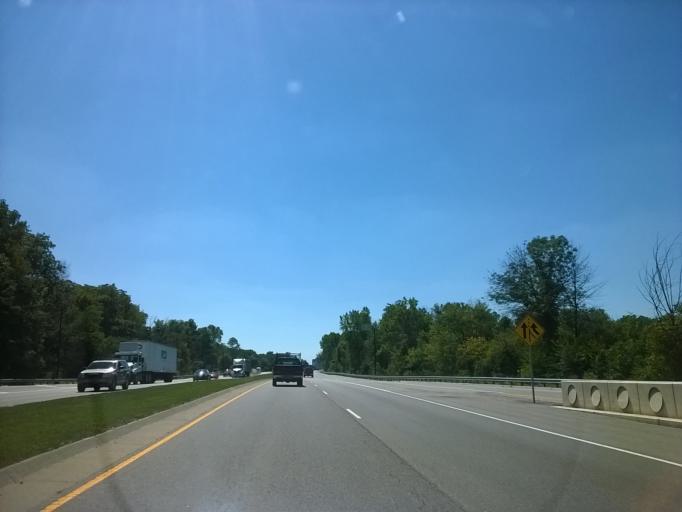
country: US
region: Indiana
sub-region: Hamilton County
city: Carmel
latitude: 39.9400
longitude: -86.1129
